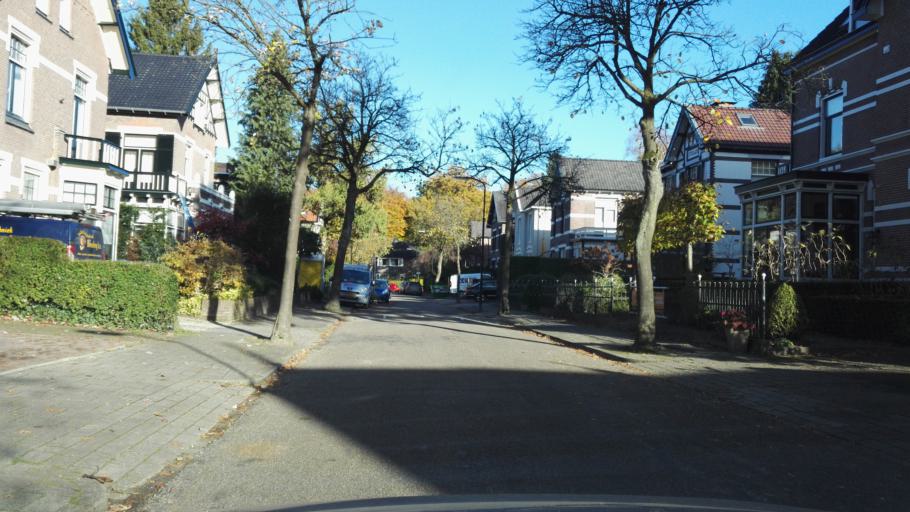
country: NL
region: Gelderland
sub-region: Gemeente Apeldoorn
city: Apeldoorn
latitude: 52.2206
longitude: 5.9676
